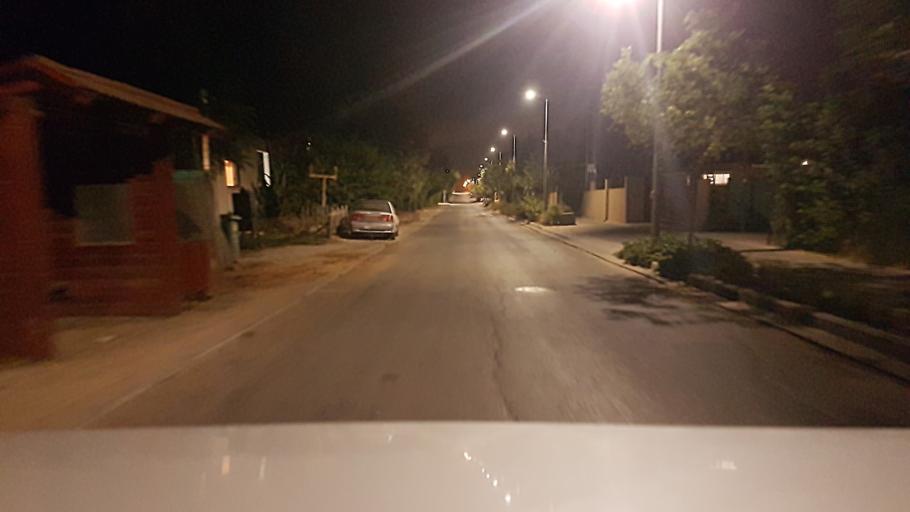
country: IL
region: Central District
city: Nehalim
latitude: 32.0751
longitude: 34.9235
